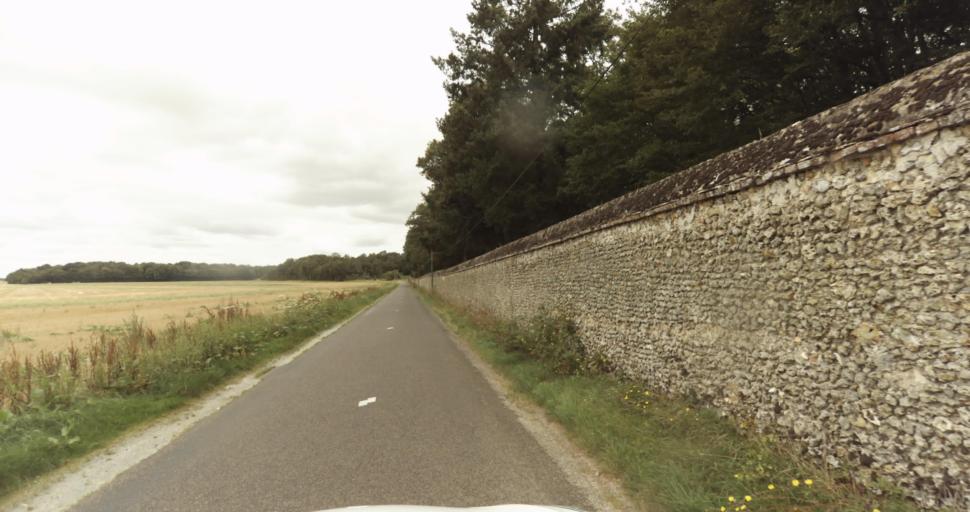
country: FR
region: Centre
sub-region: Departement d'Eure-et-Loir
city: Saint-Lubin-des-Joncherets
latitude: 48.8207
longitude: 1.2346
